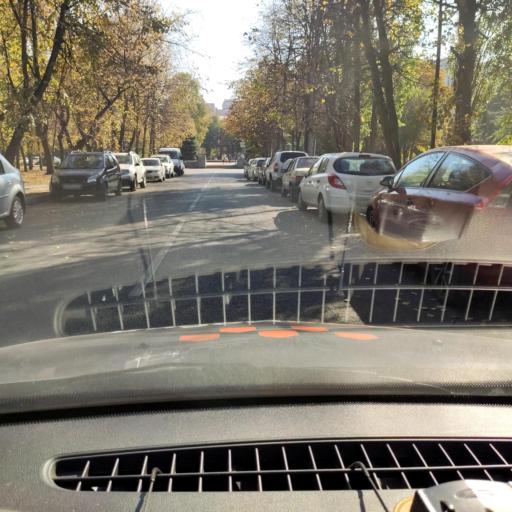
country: RU
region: Voronezj
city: Voronezh
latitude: 51.6524
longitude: 39.1735
